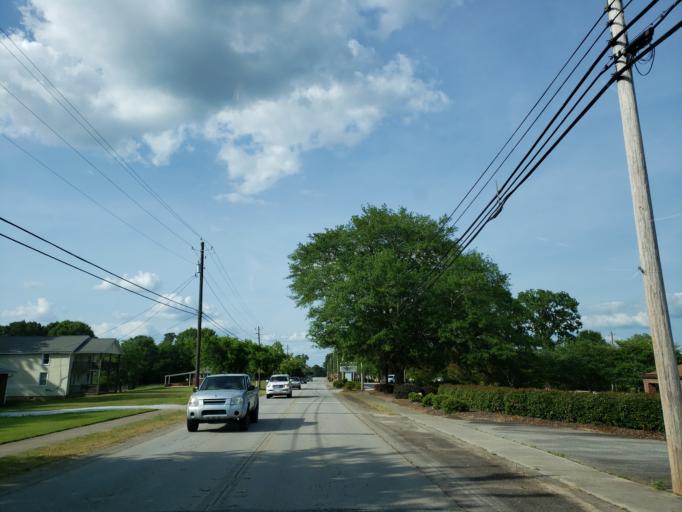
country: US
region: Georgia
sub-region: Carroll County
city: Carrollton
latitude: 33.4531
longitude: -85.1327
